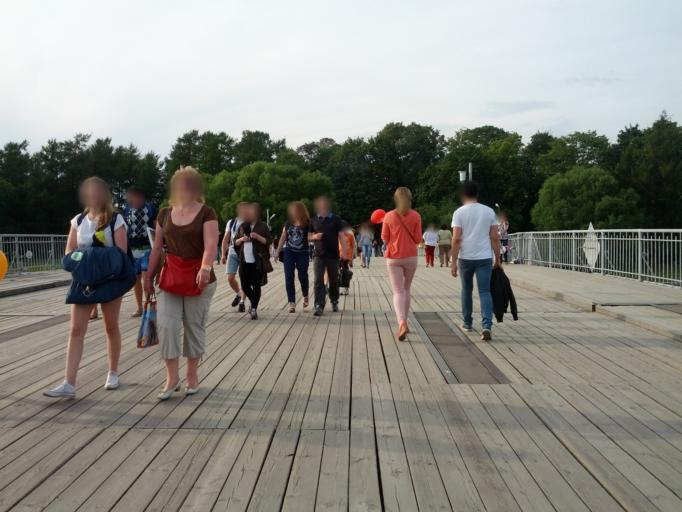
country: RU
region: Leningrad
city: Krestovskiy ostrov
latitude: 59.9754
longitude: 30.2581
